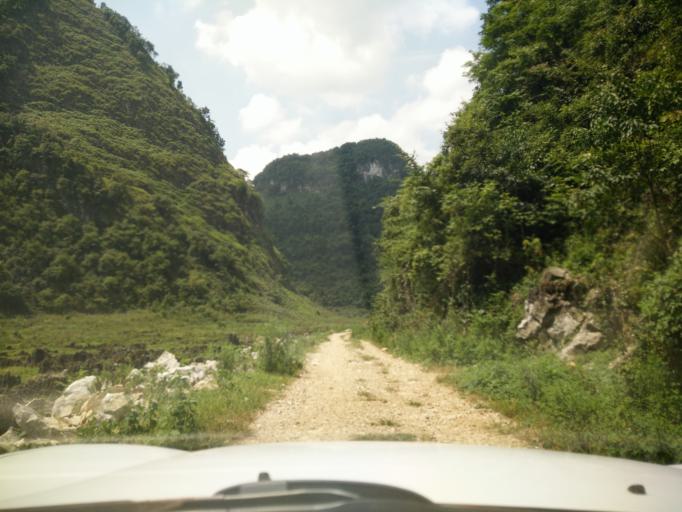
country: CN
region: Guangxi Zhuangzu Zizhiqu
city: Xinzhou
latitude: 25.0098
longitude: 105.7064
